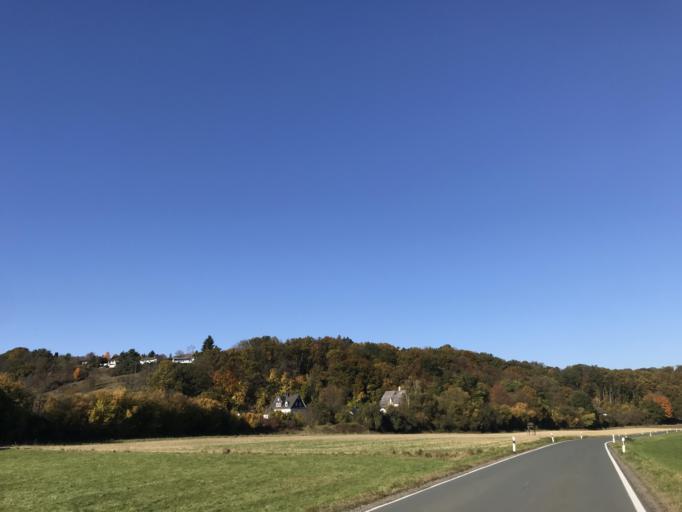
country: DE
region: Hesse
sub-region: Regierungsbezirk Giessen
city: Braunfels
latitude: 50.5135
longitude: 8.4085
